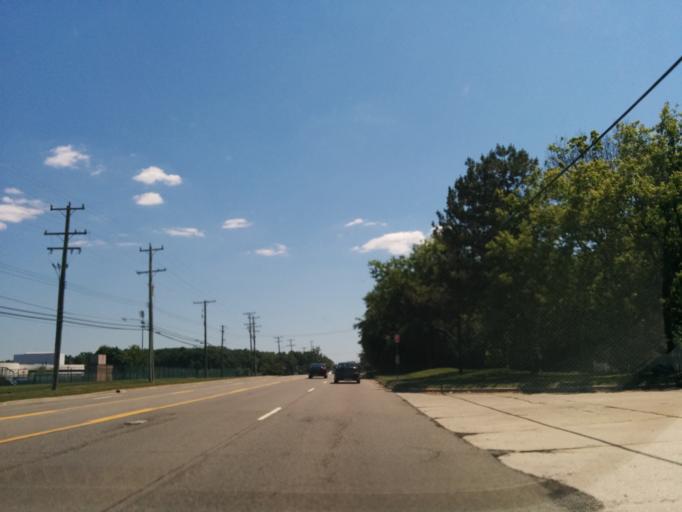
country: US
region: Michigan
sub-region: Oakland County
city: Orchard Lake
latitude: 42.5696
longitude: -83.3620
